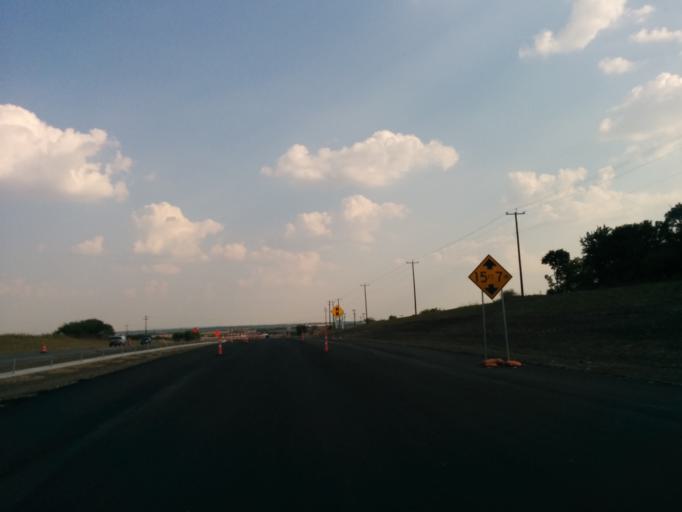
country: US
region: Texas
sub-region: Bexar County
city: Converse
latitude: 29.4704
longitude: -98.2940
